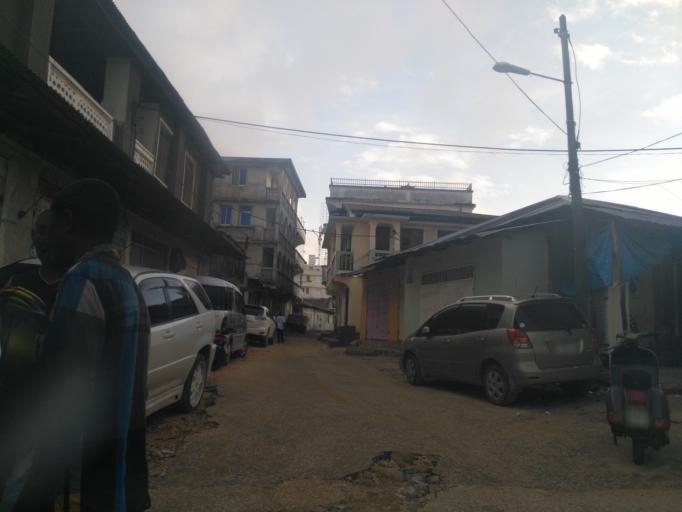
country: TZ
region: Zanzibar Urban/West
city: Zanzibar
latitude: -6.1670
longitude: 39.1972
